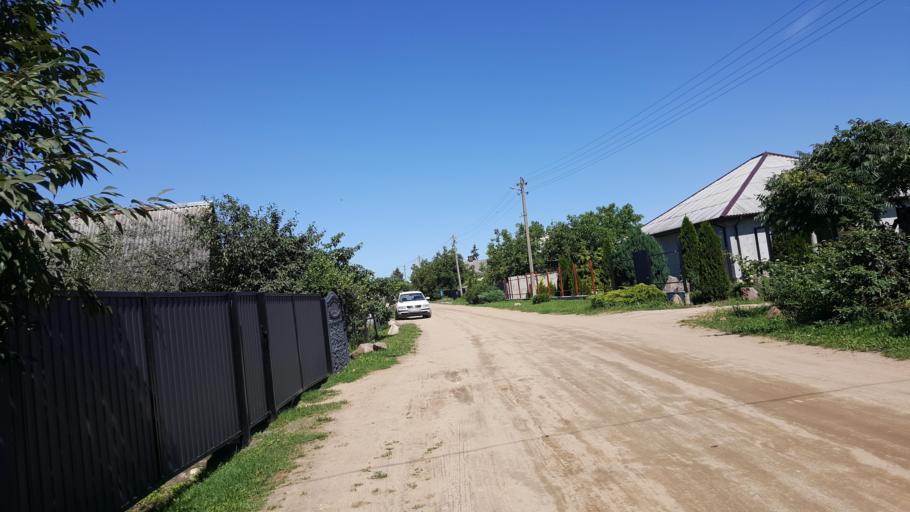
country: BY
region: Brest
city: Charnawchytsy
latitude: 52.2285
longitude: 23.7798
